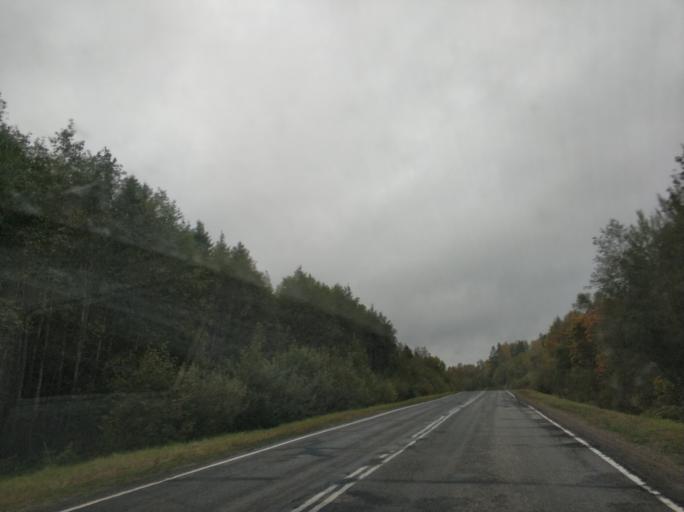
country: RU
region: Pskov
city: Sebezh
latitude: 56.2081
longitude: 28.6425
